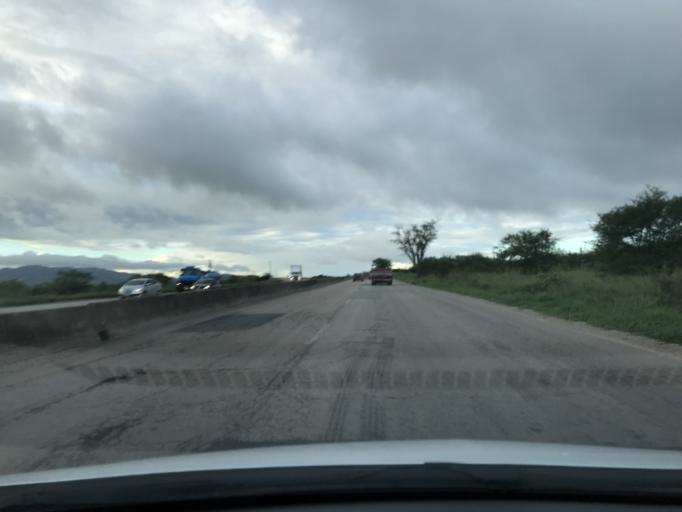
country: BR
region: Pernambuco
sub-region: Bezerros
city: Bezerros
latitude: -8.2908
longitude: -35.8223
